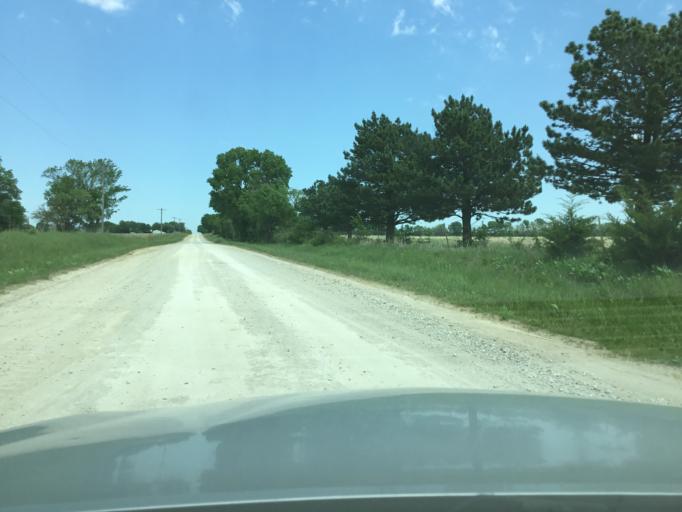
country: US
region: Kansas
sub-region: Montgomery County
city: Independence
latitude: 37.0952
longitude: -95.7829
